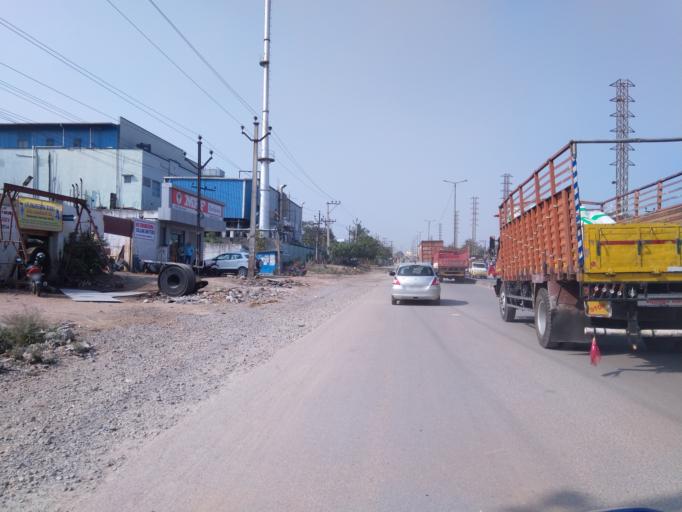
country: IN
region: Telangana
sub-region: Rangareddi
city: Quthbullapur
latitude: 17.5327
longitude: 78.4358
